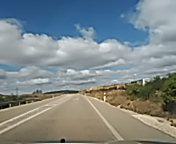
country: ES
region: Castille and Leon
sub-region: Provincia de Burgos
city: Hontoria del Pinar
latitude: 41.8512
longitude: -3.1746
